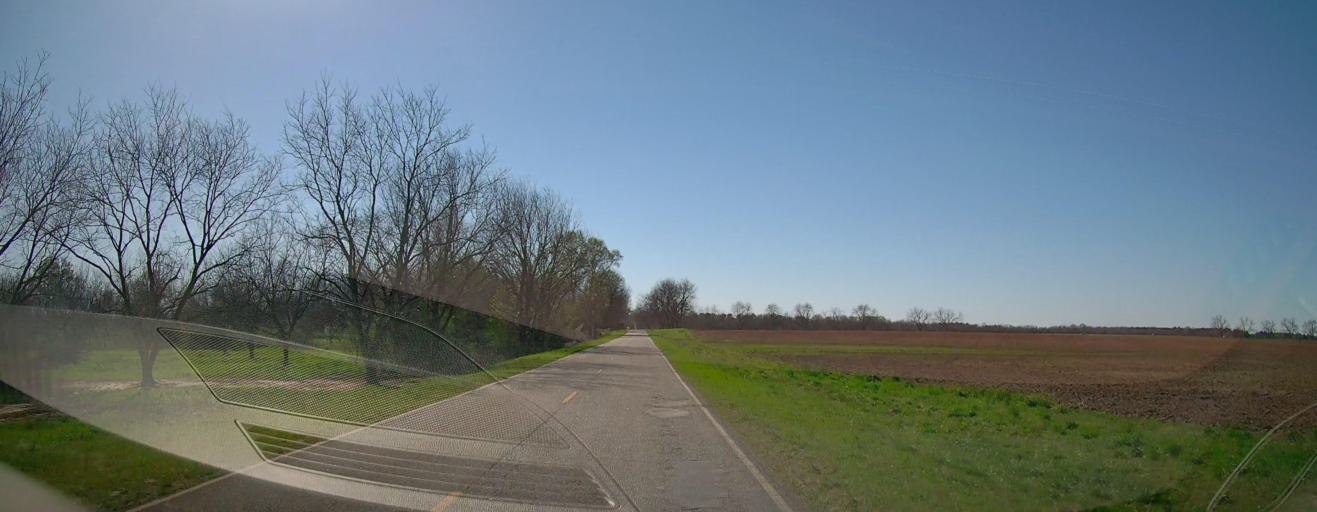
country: US
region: Georgia
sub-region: Peach County
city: Fort Valley
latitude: 32.6442
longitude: -83.8587
